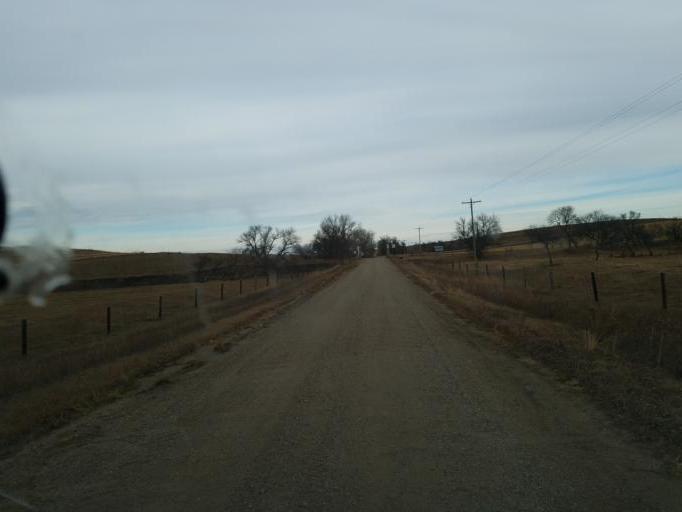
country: US
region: Nebraska
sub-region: Knox County
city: Bloomfield
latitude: 42.5541
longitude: -97.7206
